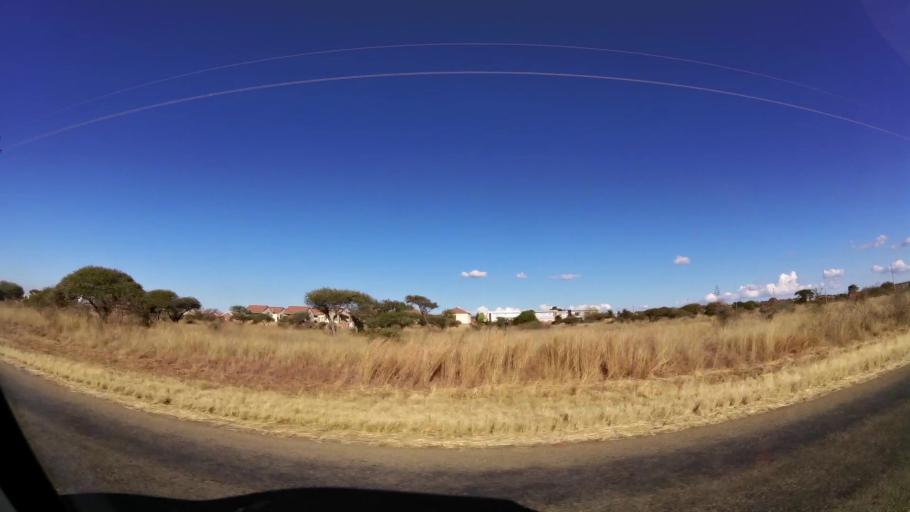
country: ZA
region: Limpopo
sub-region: Capricorn District Municipality
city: Polokwane
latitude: -23.8735
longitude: 29.4815
